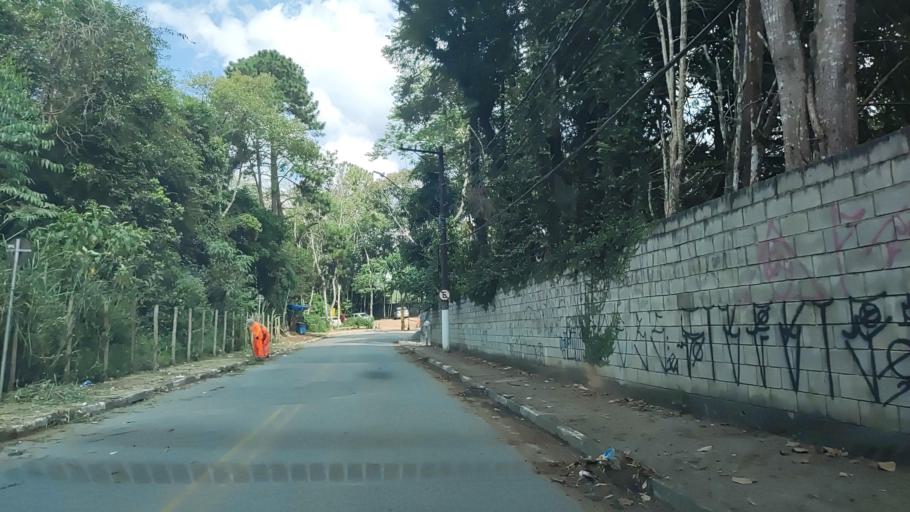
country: BR
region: Sao Paulo
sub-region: Itapecerica Da Serra
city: Itapecerica da Serra
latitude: -23.6990
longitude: -46.8462
